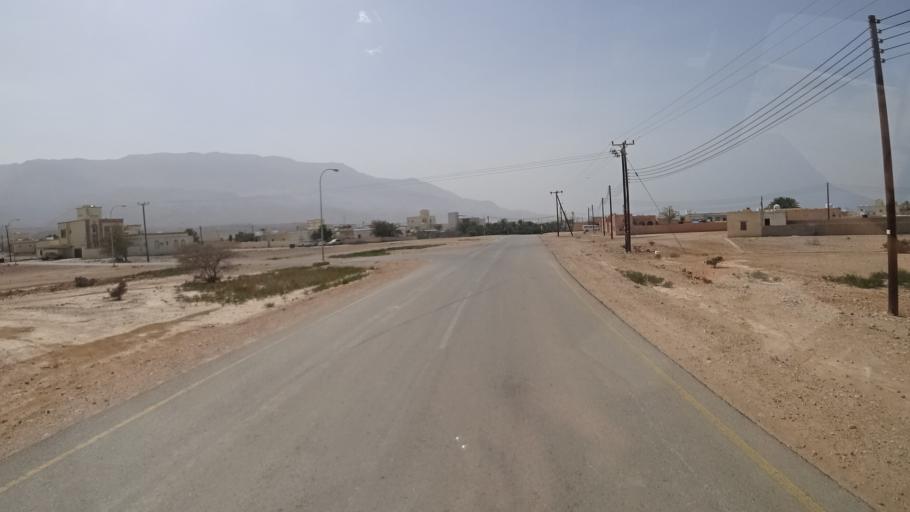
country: OM
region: Ash Sharqiyah
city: Sur
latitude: 22.9880
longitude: 59.1408
